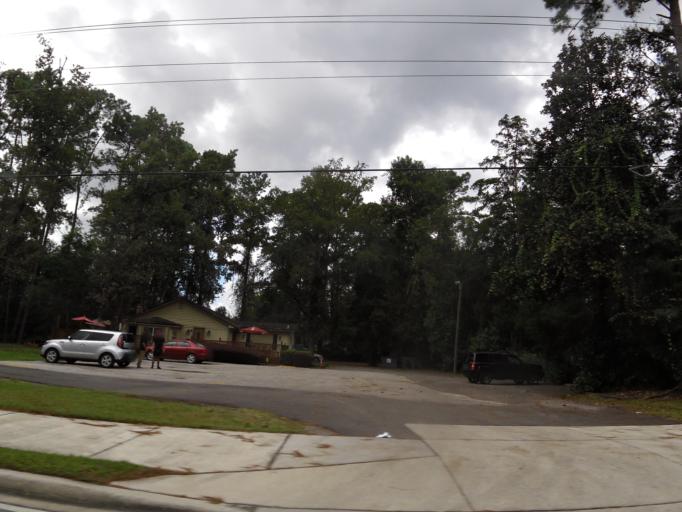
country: US
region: Florida
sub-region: Clay County
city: Asbury Lake
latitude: 30.0920
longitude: -81.8098
